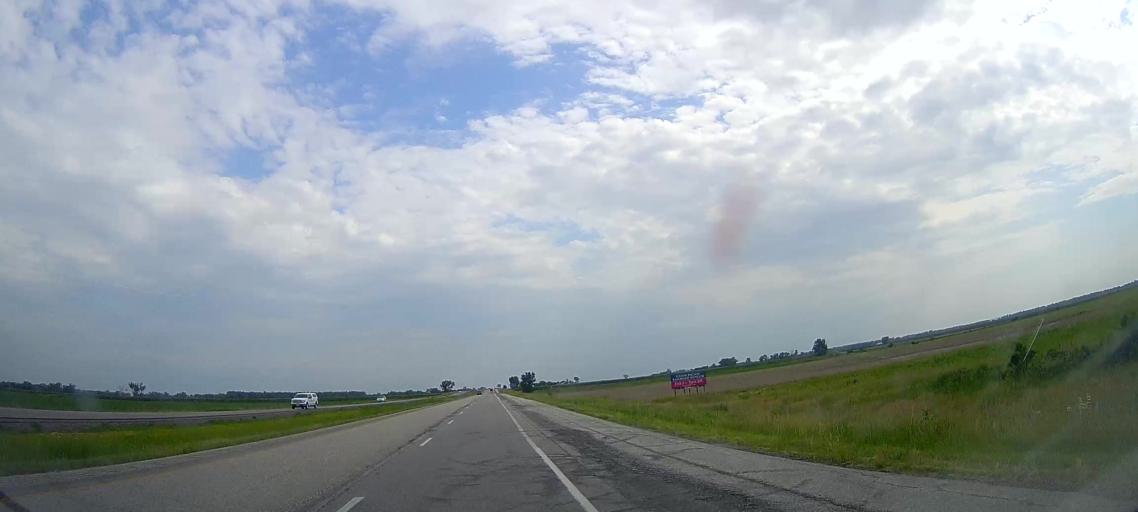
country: US
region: Nebraska
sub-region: Burt County
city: Tekamah
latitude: 41.7573
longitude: -96.0457
